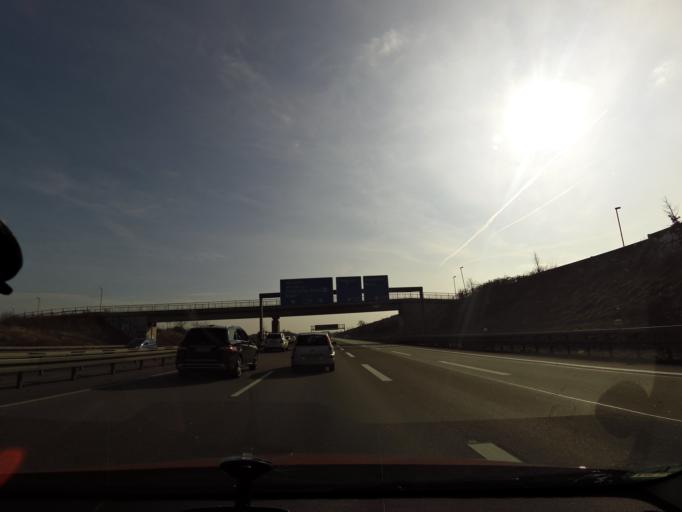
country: DE
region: Hesse
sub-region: Regierungsbezirk Darmstadt
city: Hochheim am Main
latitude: 50.0654
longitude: 8.3796
